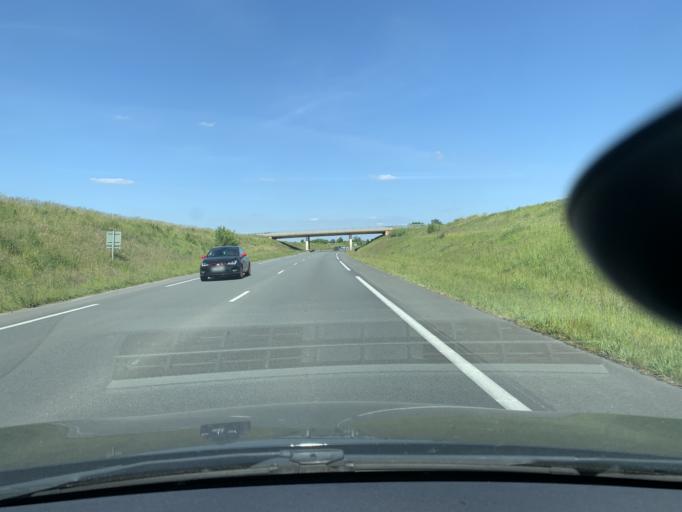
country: FR
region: Nord-Pas-de-Calais
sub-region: Departement du Nord
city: Cambrai
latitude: 50.1505
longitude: 3.2460
